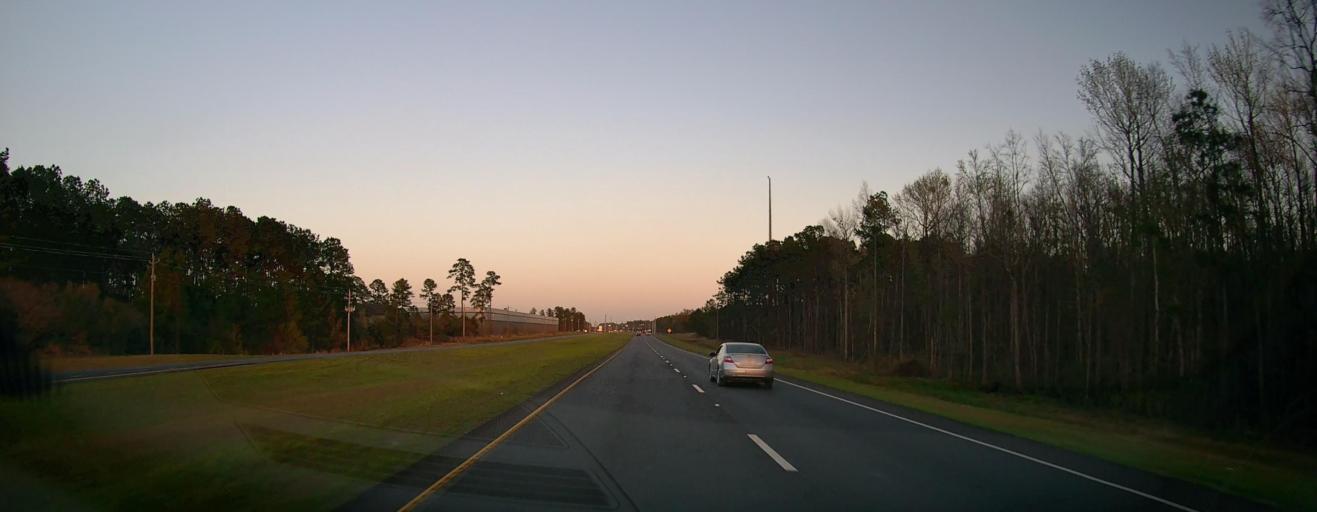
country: US
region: Georgia
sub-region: Chatham County
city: Pooler
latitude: 32.1623
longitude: -81.2540
